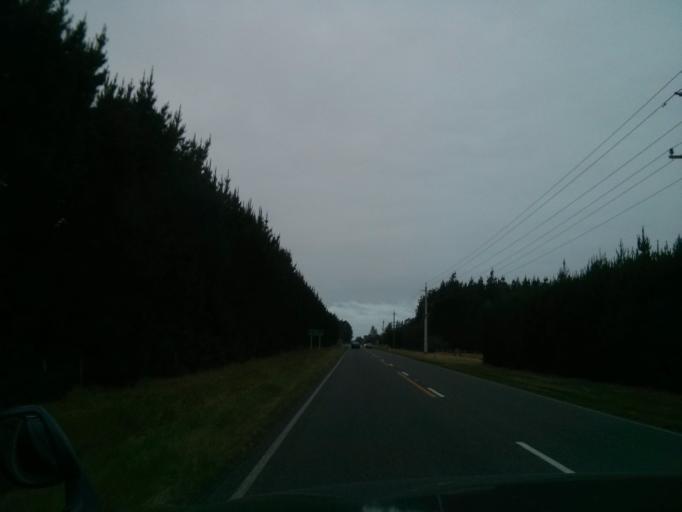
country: NZ
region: Canterbury
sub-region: Waimakariri District
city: Kaiapoi
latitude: -43.3781
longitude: 172.5301
